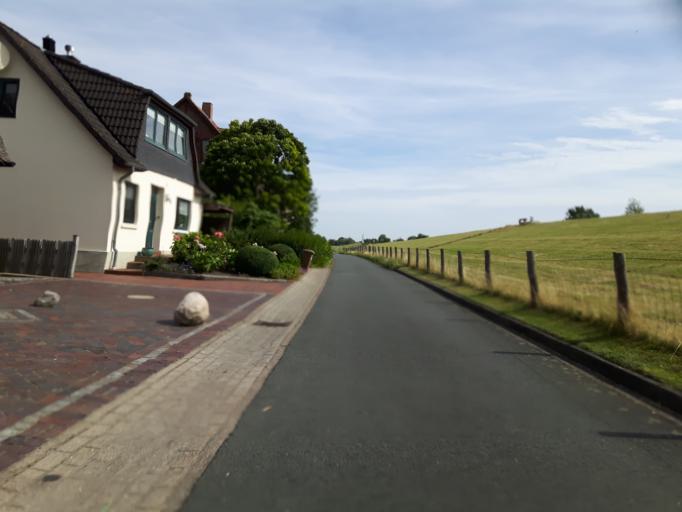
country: DE
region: Lower Saxony
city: Elsfleth
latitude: 53.2539
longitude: 8.4736
